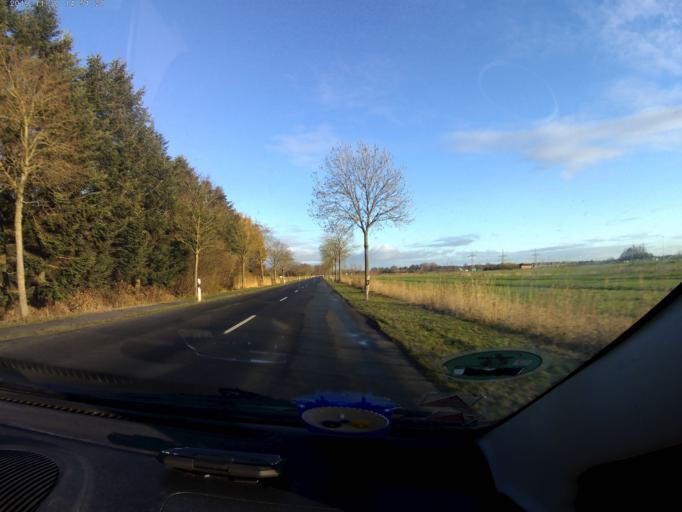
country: DE
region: Lower Saxony
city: Jemgum
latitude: 53.2618
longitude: 7.4168
